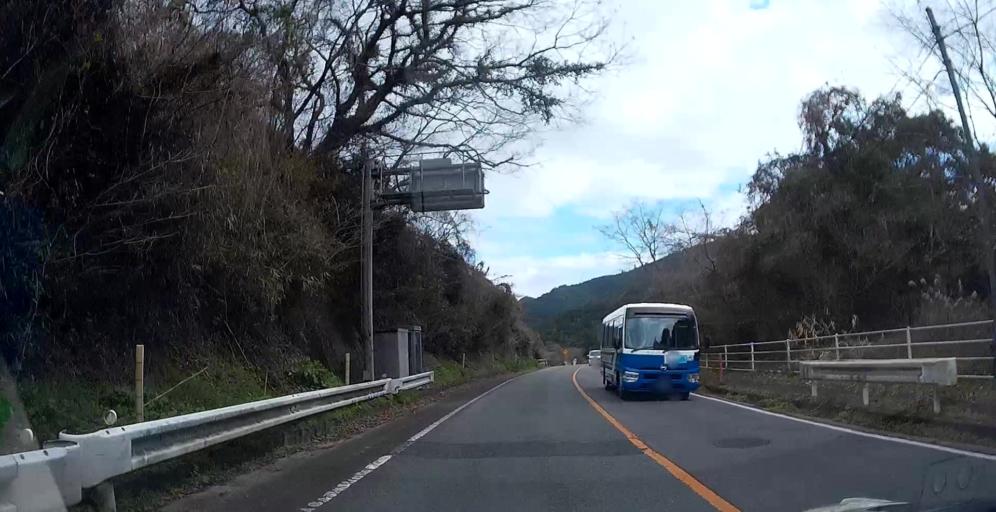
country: JP
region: Kumamoto
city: Minamata
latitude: 32.3371
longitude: 130.4894
